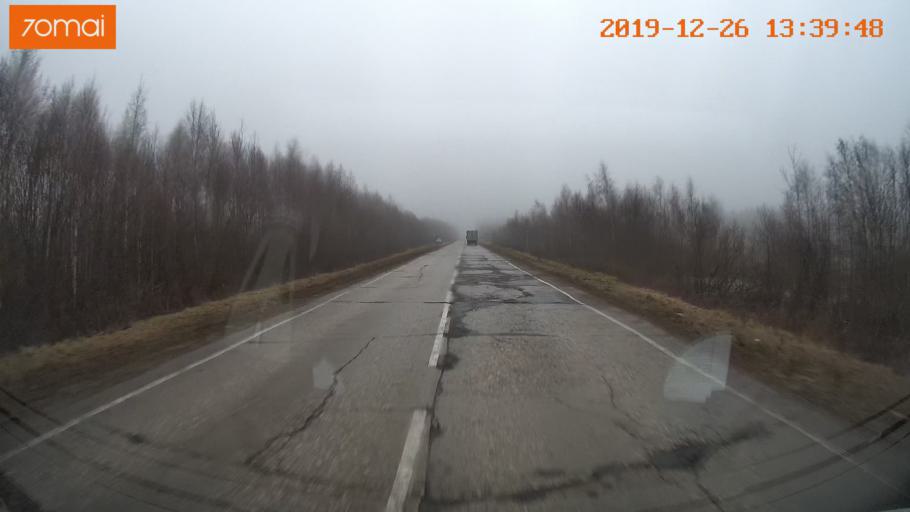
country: RU
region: Vologda
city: Sheksna
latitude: 58.7486
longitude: 38.4180
